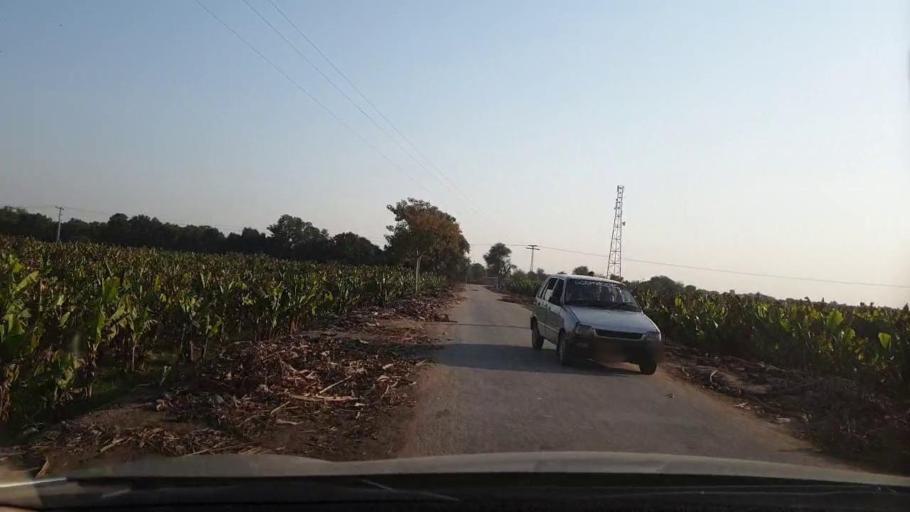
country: PK
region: Sindh
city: Berani
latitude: 25.6413
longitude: 68.8084
